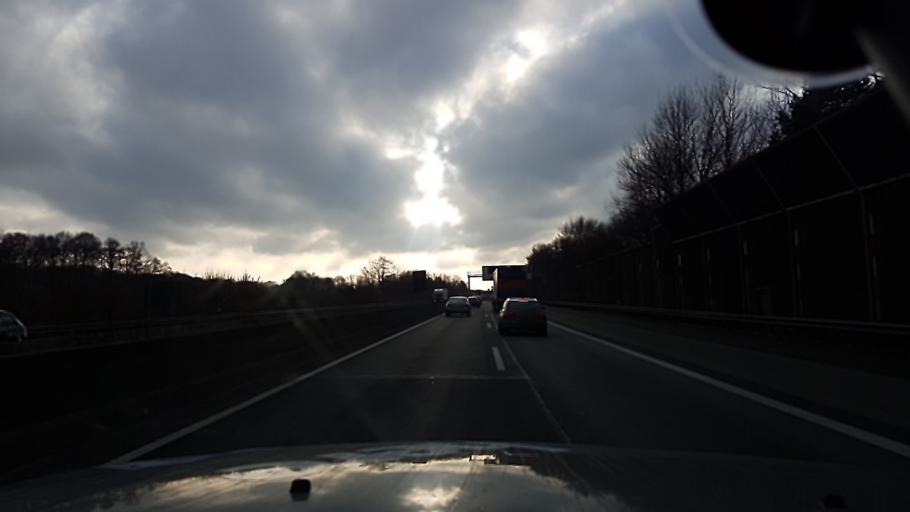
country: DE
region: North Rhine-Westphalia
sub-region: Regierungsbezirk Munster
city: Lotte
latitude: 52.2831
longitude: 7.9374
